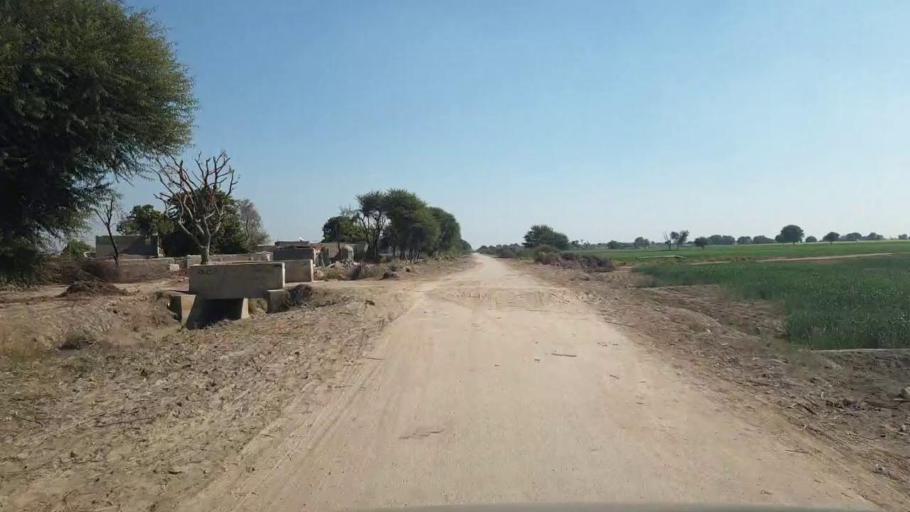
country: PK
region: Sindh
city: Shahpur Chakar
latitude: 26.1389
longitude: 68.6585
